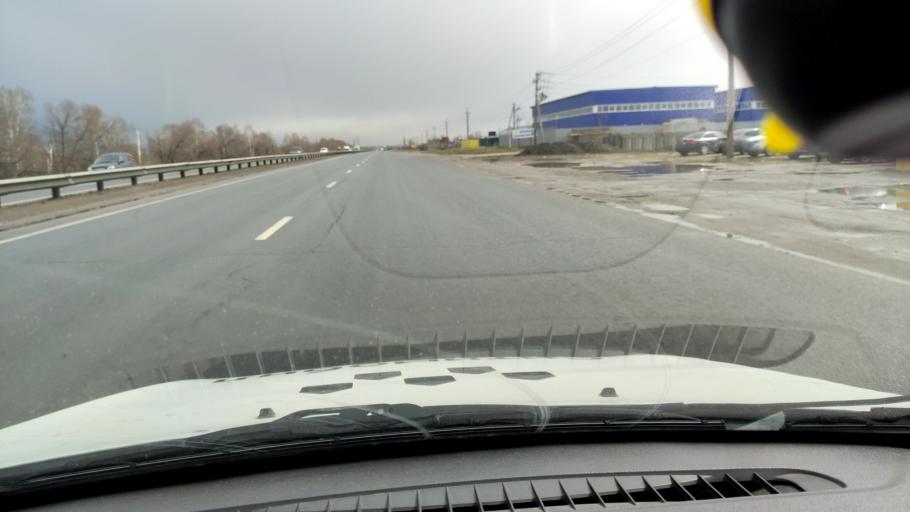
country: RU
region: Samara
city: Tol'yatti
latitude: 53.5789
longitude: 49.4133
